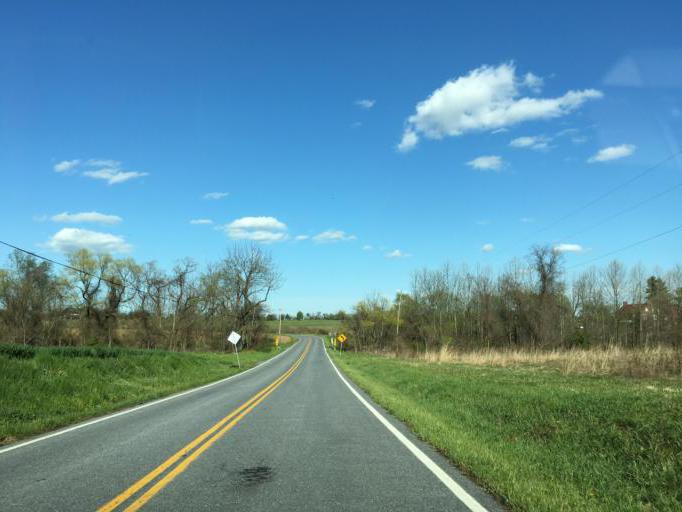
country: US
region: Maryland
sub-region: Frederick County
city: Emmitsburg
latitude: 39.6606
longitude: -77.3562
